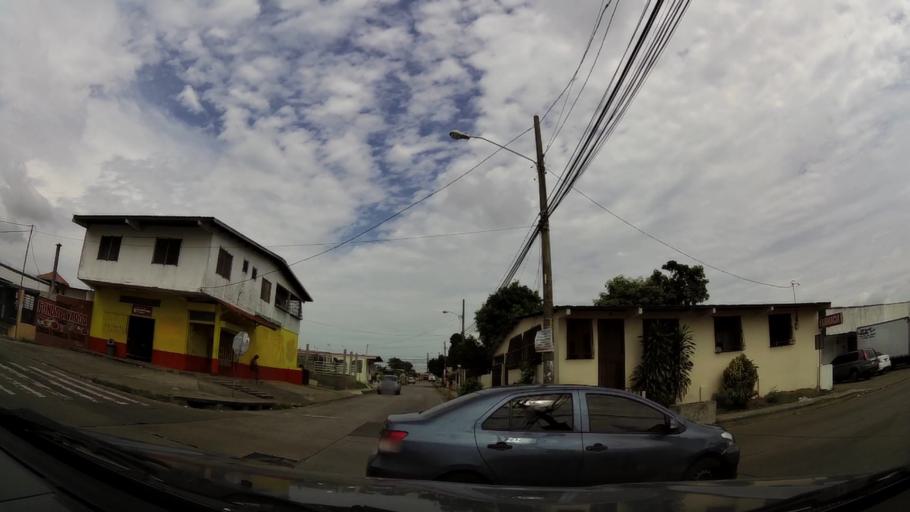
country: PA
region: Panama
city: Tocumen
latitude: 9.0510
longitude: -79.4146
